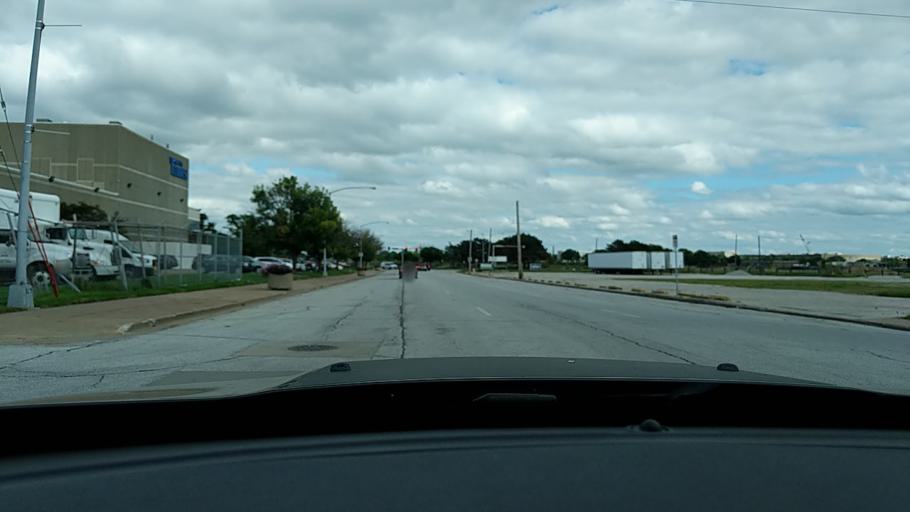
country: US
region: Iowa
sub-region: Scott County
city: Davenport
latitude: 41.5224
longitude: -90.5683
